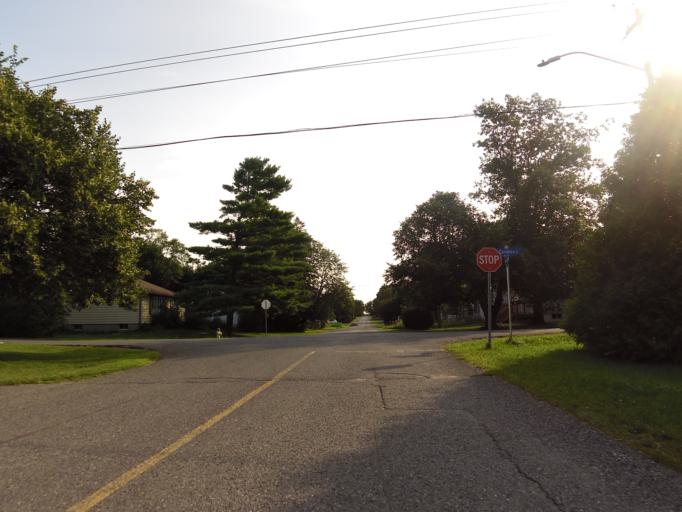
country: CA
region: Ontario
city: Ottawa
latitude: 45.3510
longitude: -75.7447
